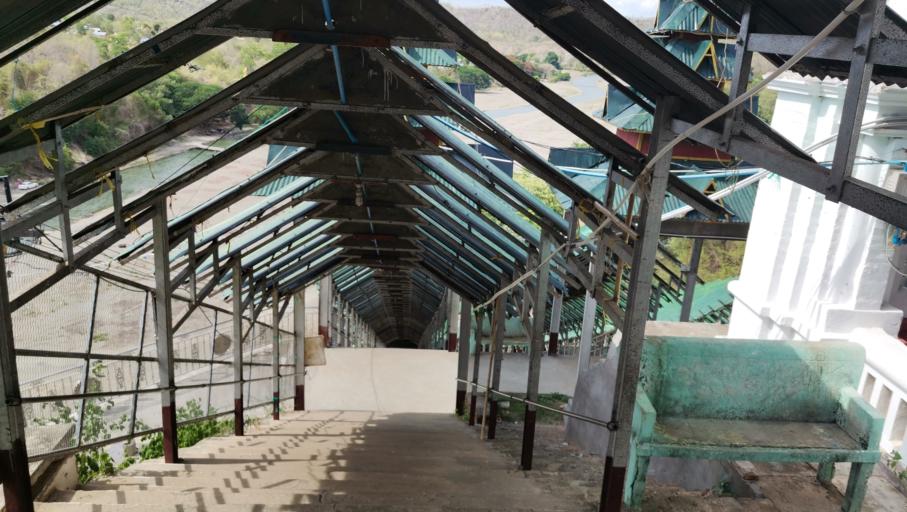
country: MM
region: Magway
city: Minbu
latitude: 20.1014
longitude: 94.5273
